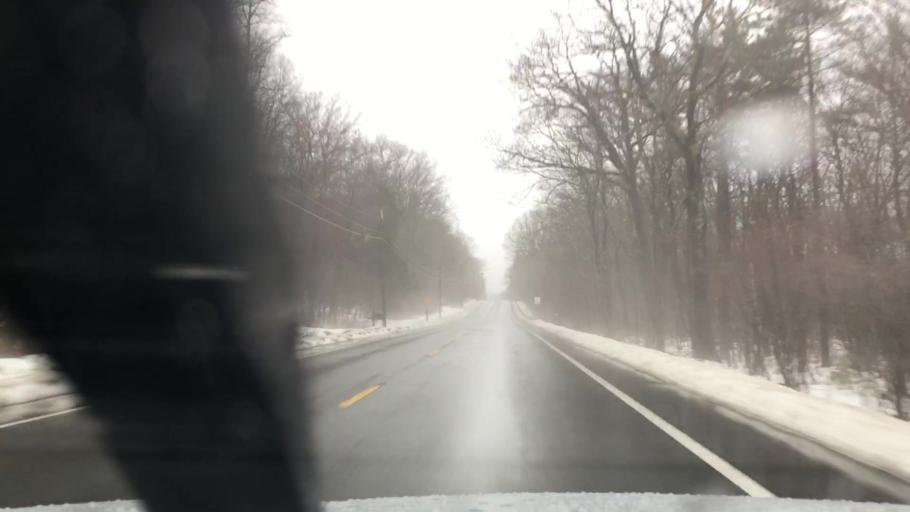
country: US
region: Massachusetts
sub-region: Hampshire County
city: Pelham
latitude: 42.3851
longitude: -72.4018
